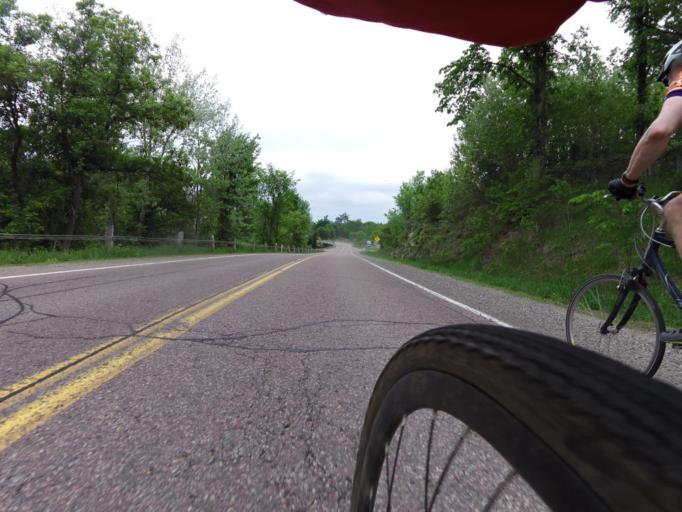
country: CA
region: Ontario
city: Renfrew
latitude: 45.2980
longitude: -76.7160
